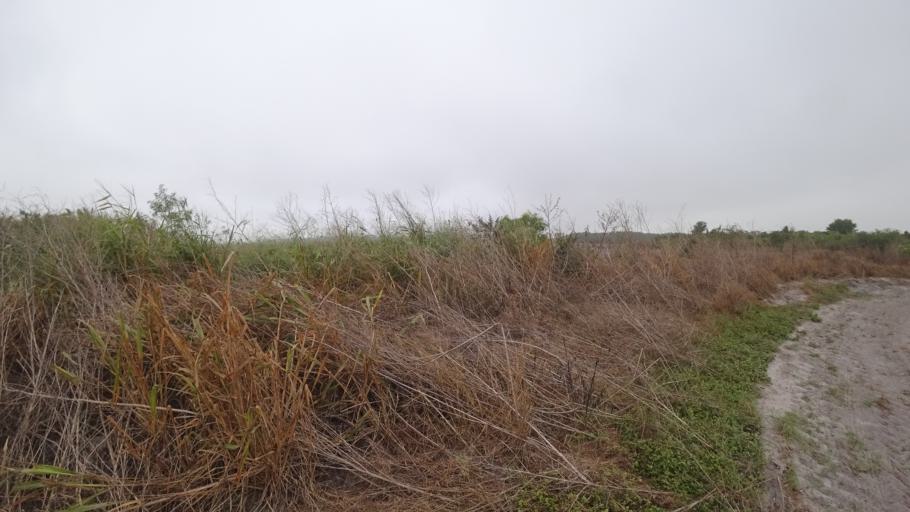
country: US
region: Florida
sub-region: Sarasota County
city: Warm Mineral Springs
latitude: 27.2993
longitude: -82.1707
